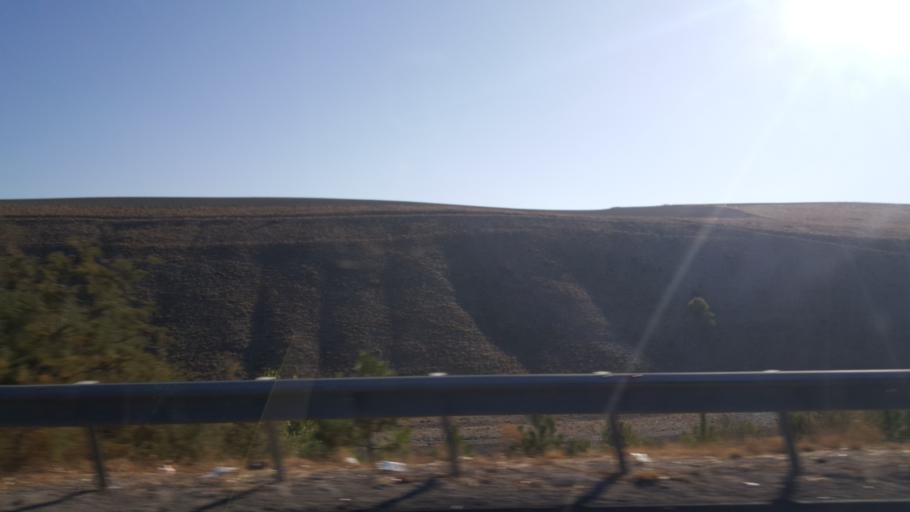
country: TR
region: Ankara
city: Cankaya
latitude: 39.8496
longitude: 32.8928
